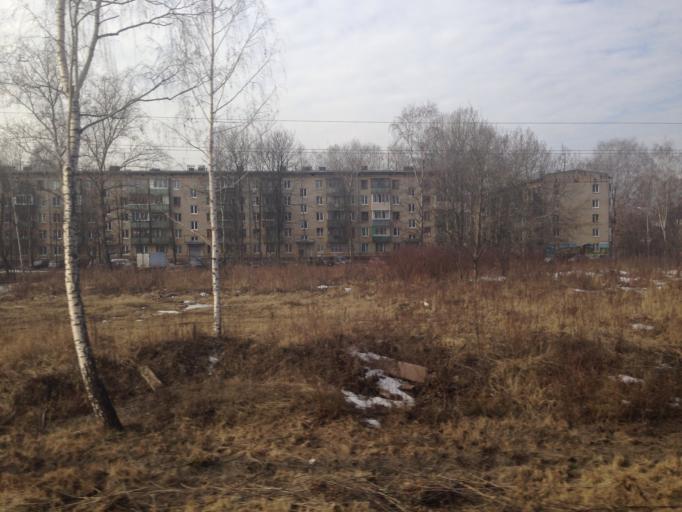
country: RU
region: Moskovskaya
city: Dolgoprudnyy
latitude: 55.9455
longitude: 37.5172
